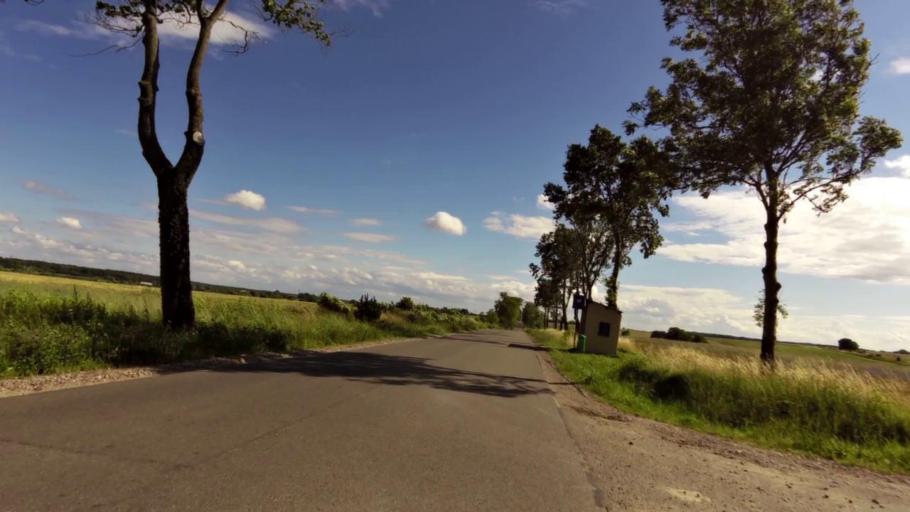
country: PL
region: West Pomeranian Voivodeship
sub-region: Powiat slawienski
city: Slawno
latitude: 54.4483
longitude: 16.7368
